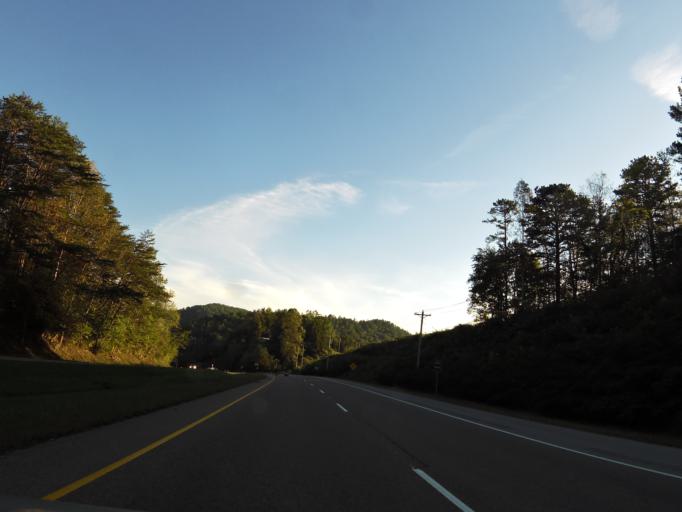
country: US
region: Tennessee
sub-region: Blount County
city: Wildwood
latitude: 35.7168
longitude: -83.8205
